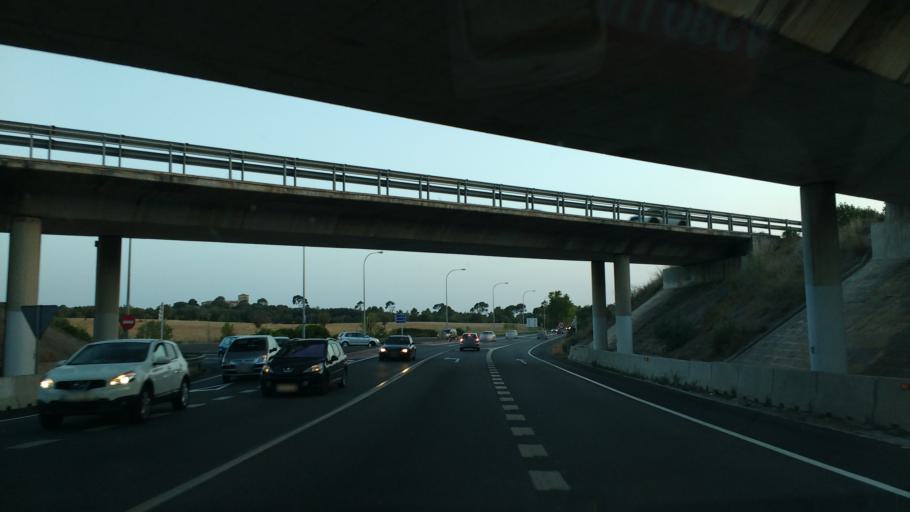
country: ES
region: Balearic Islands
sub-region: Illes Balears
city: Marratxi
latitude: 39.6301
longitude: 2.7364
